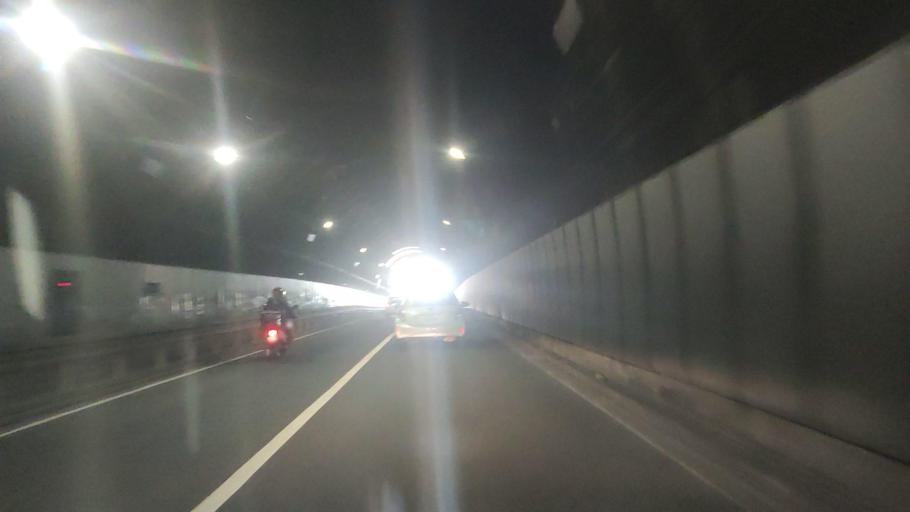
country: JP
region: Oita
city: Oita
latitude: 33.2213
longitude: 131.5949
